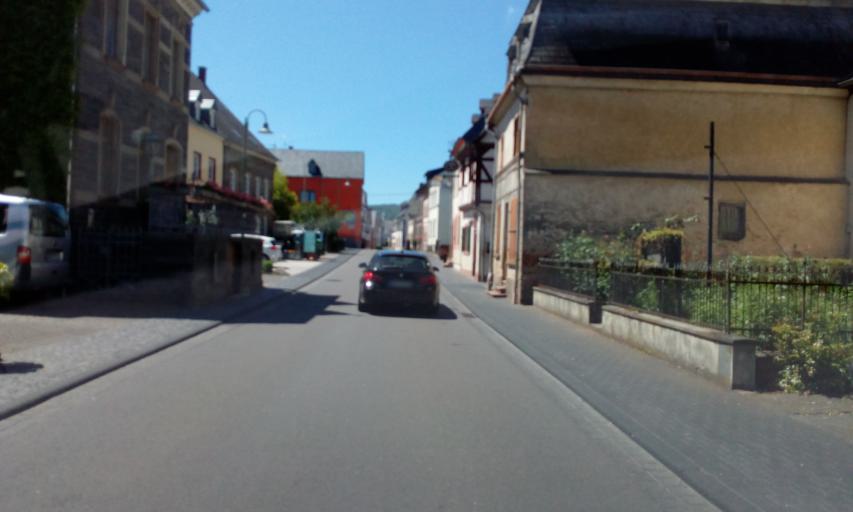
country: DE
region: Rheinland-Pfalz
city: Brauneberg
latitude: 49.9095
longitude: 6.9881
